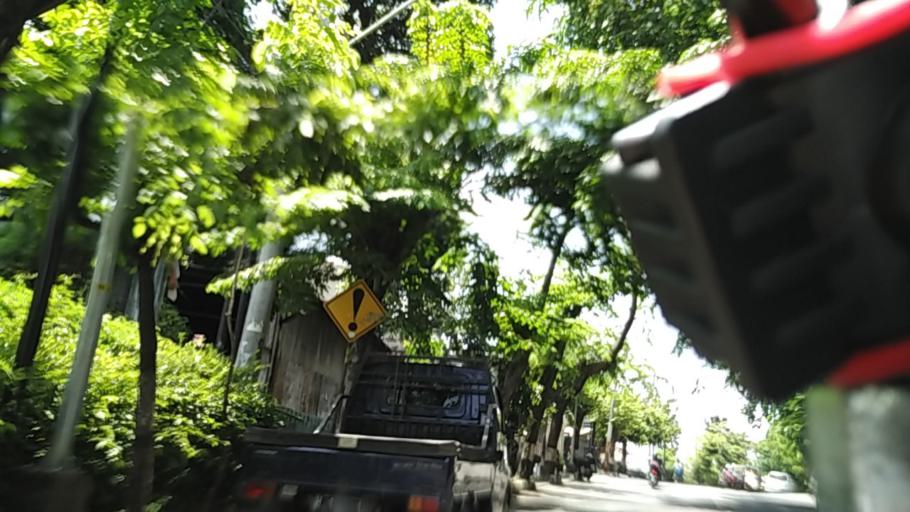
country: ID
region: Central Java
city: Semarang
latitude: -6.9906
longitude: 110.3821
